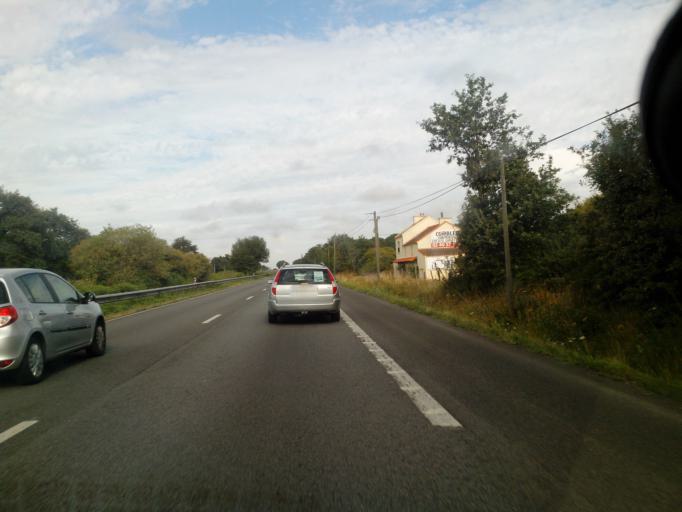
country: FR
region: Pays de la Loire
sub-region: Departement de la Loire-Atlantique
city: Le Temple-de-Bretagne
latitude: 47.3380
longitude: -1.8105
